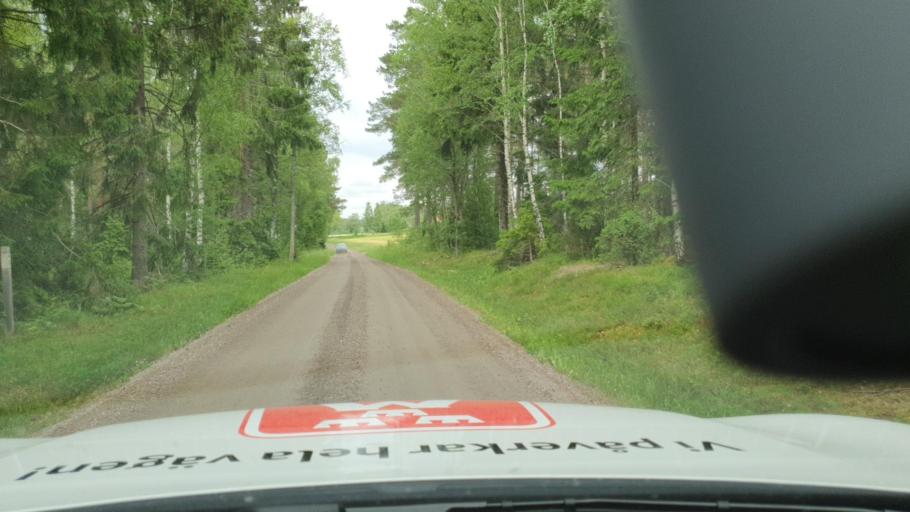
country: SE
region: Vaestra Goetaland
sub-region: Tidaholms Kommun
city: Tidaholm
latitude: 58.1668
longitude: 14.0470
